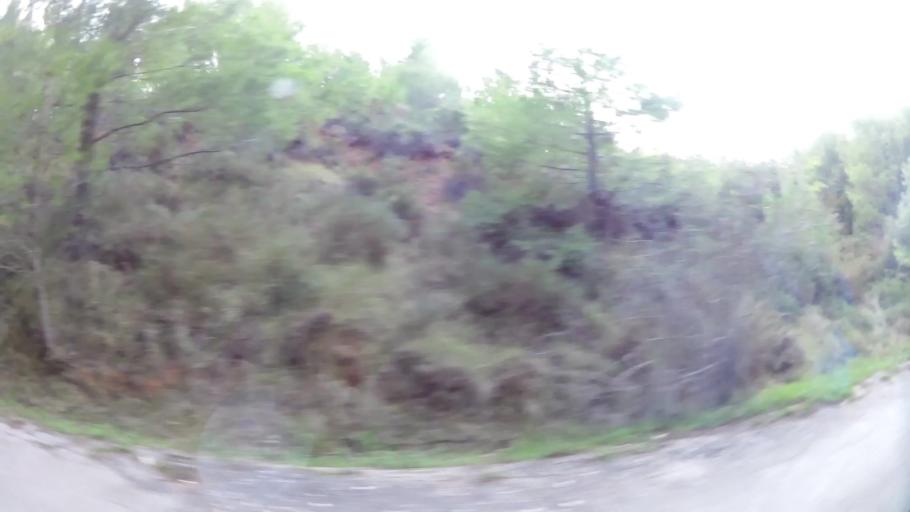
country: GR
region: Attica
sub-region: Nomarchia Anatolikis Attikis
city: Kryoneri
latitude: 38.1487
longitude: 23.8349
